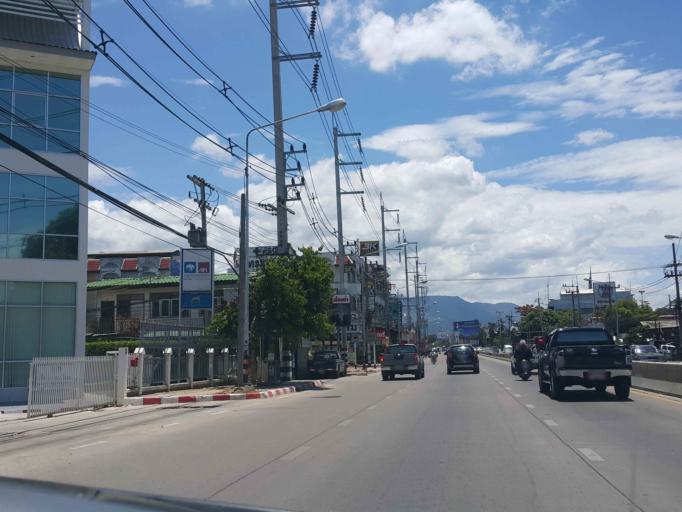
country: TH
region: Chiang Mai
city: Chiang Mai
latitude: 18.7576
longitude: 99.0001
